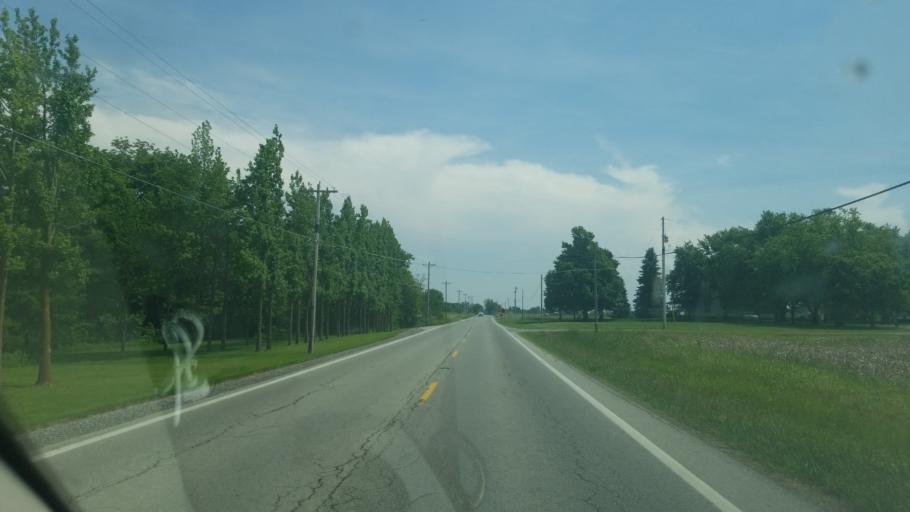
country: US
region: Ohio
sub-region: Logan County
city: Northwood
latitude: 40.4834
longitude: -83.7403
